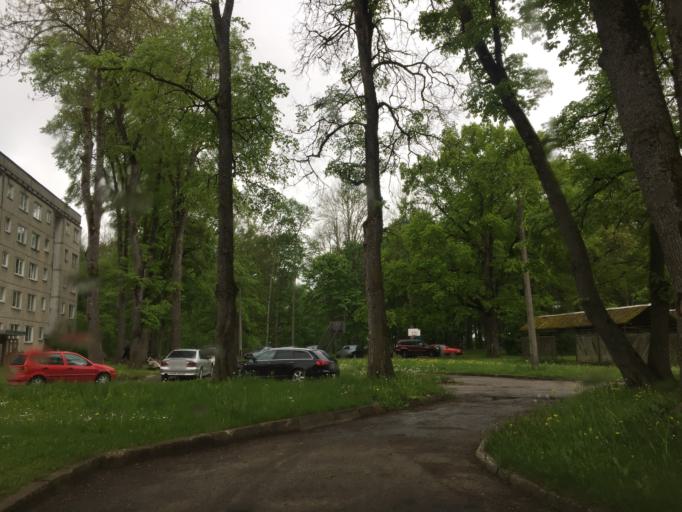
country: LV
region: Lielvarde
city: Lielvarde
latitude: 56.7132
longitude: 24.8358
